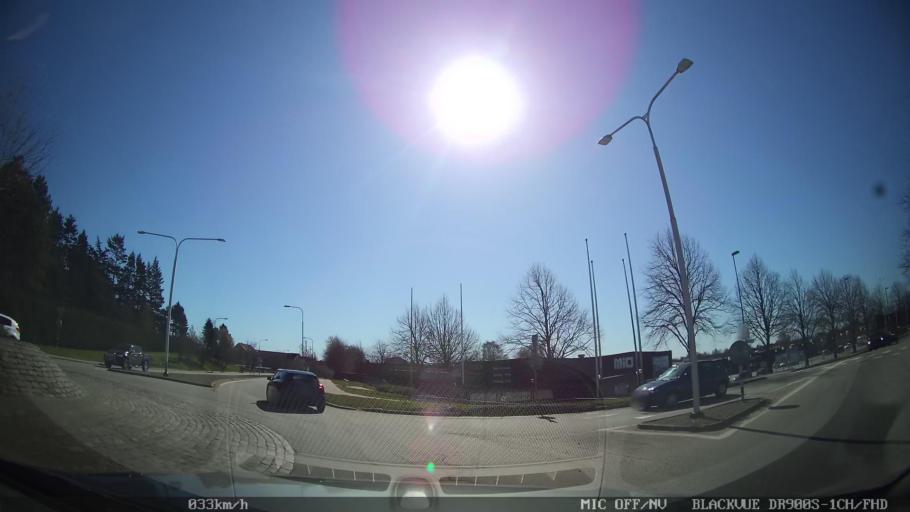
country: SE
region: Skane
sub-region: Ystads Kommun
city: Ystad
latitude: 55.4332
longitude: 13.8012
